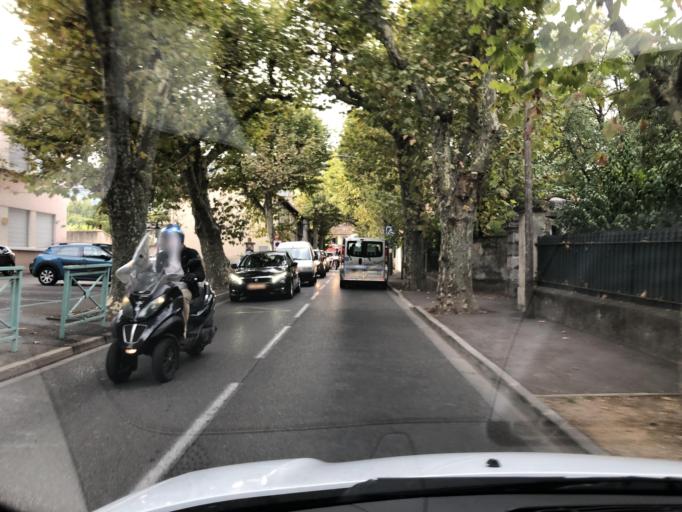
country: FR
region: Provence-Alpes-Cote d'Azur
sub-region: Departement des Bouches-du-Rhone
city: La Penne-sur-Huveaune
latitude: 43.2829
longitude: 5.5150
